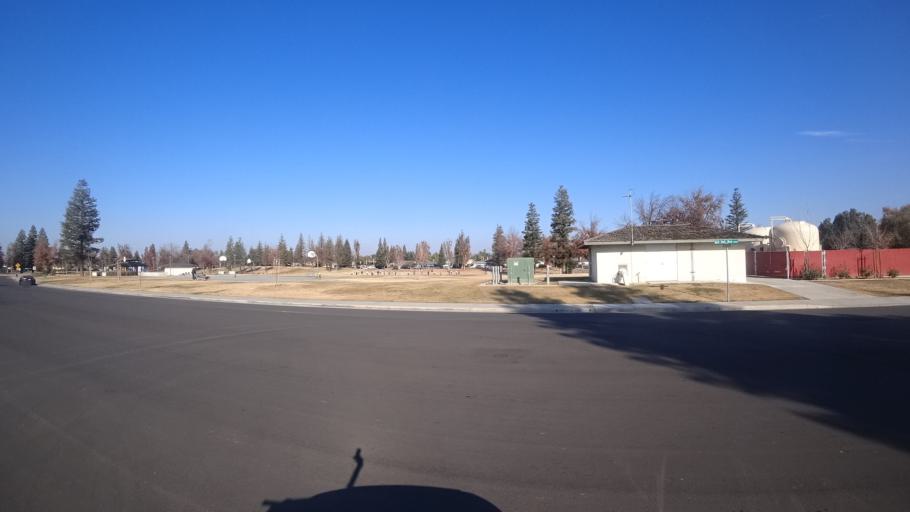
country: US
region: California
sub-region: Kern County
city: Greenacres
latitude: 35.3260
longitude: -119.1049
